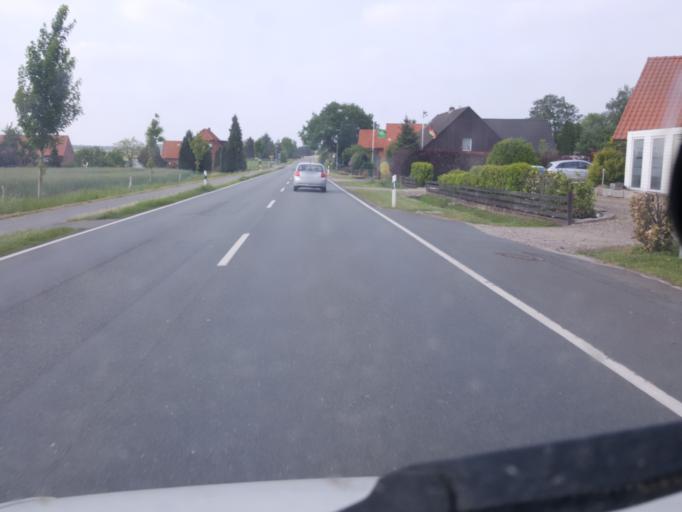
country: DE
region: Lower Saxony
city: Binnen
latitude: 52.6270
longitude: 9.1285
